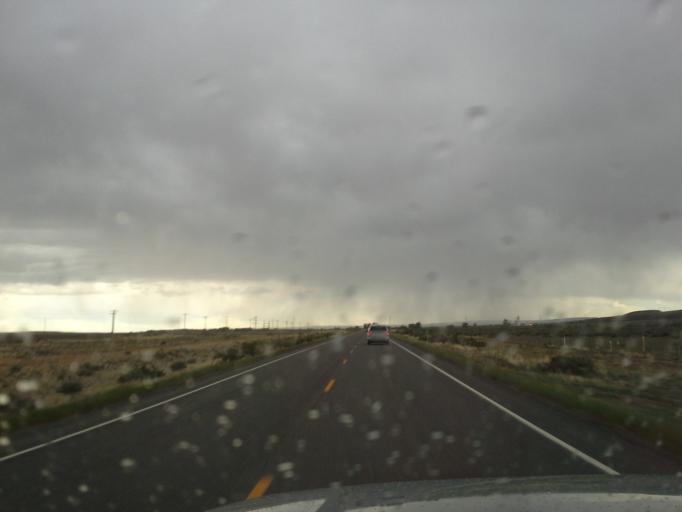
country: US
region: Wyoming
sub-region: Park County
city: Powell
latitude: 45.0192
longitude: -108.6295
